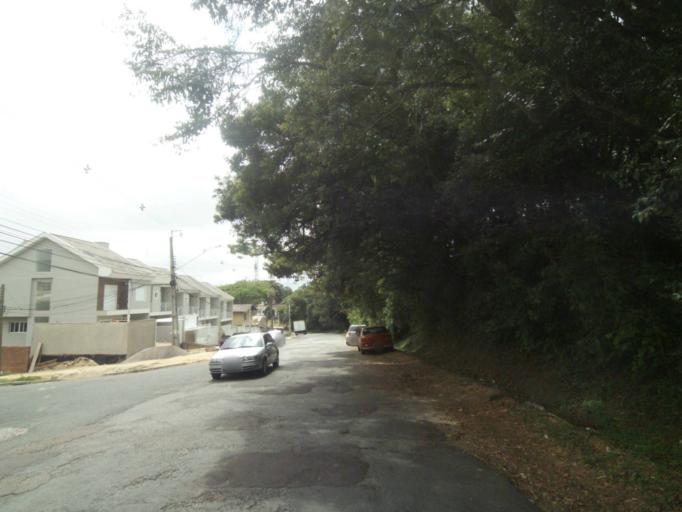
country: BR
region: Parana
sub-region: Curitiba
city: Curitiba
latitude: -25.3937
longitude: -49.2824
